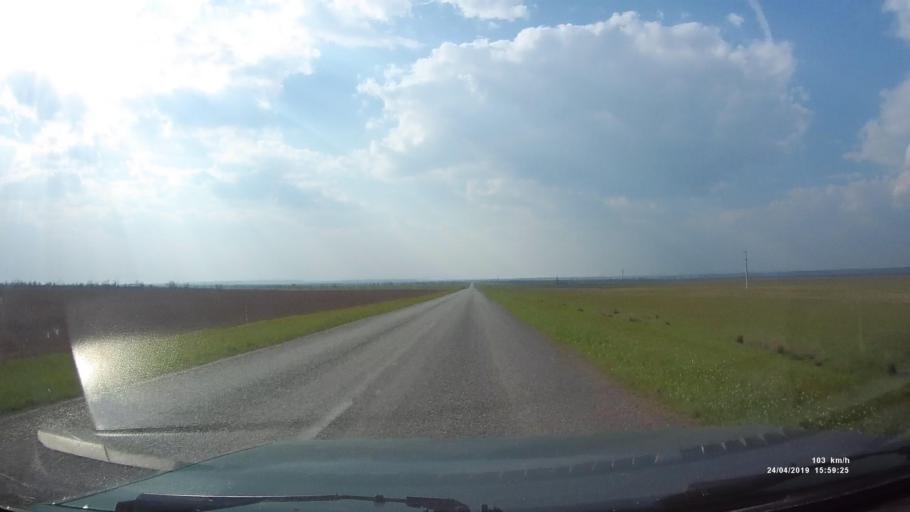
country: RU
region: Rostov
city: Sovetskoye
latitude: 46.6231
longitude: 42.4726
